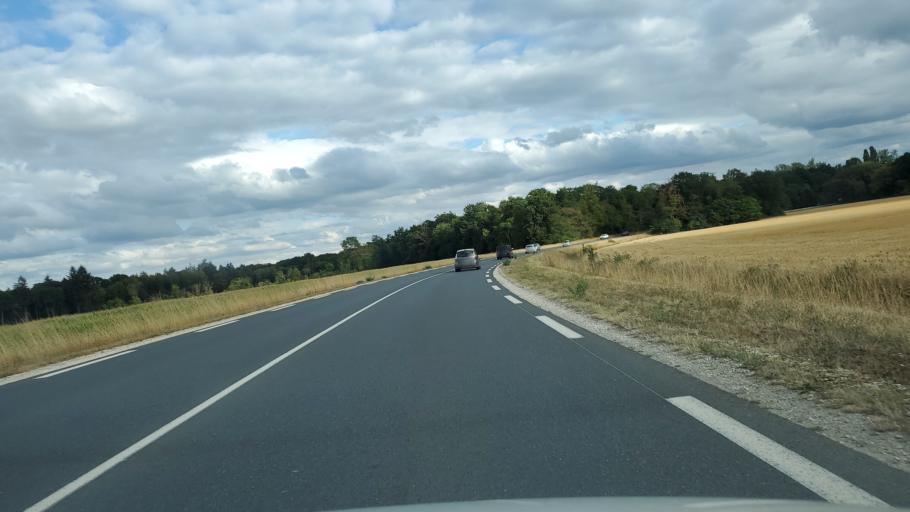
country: FR
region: Ile-de-France
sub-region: Departement de Seine-et-Marne
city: Villeneuve-le-Comte
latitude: 48.8225
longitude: 2.8398
